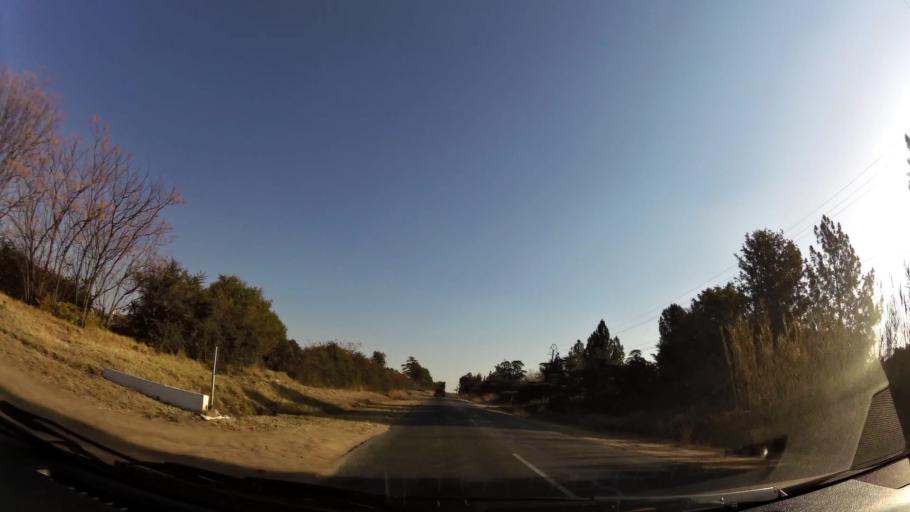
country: ZA
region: Gauteng
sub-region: West Rand District Municipality
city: Muldersdriseloop
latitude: -26.0162
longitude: 27.8856
